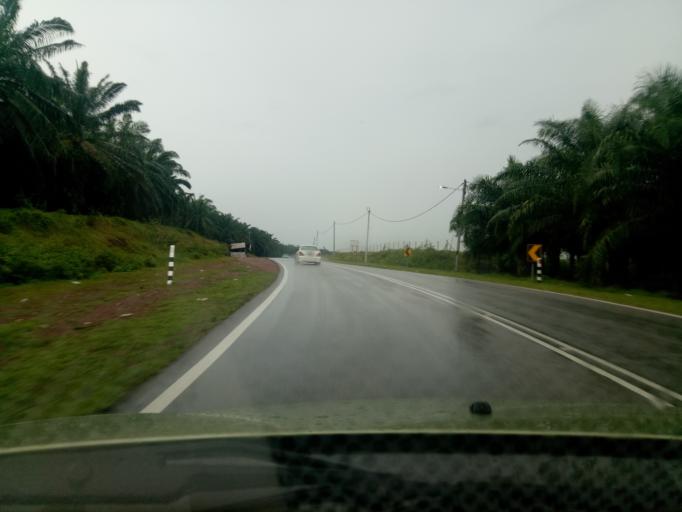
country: MY
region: Penang
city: Tasek Glugor
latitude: 5.5156
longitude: 100.5794
